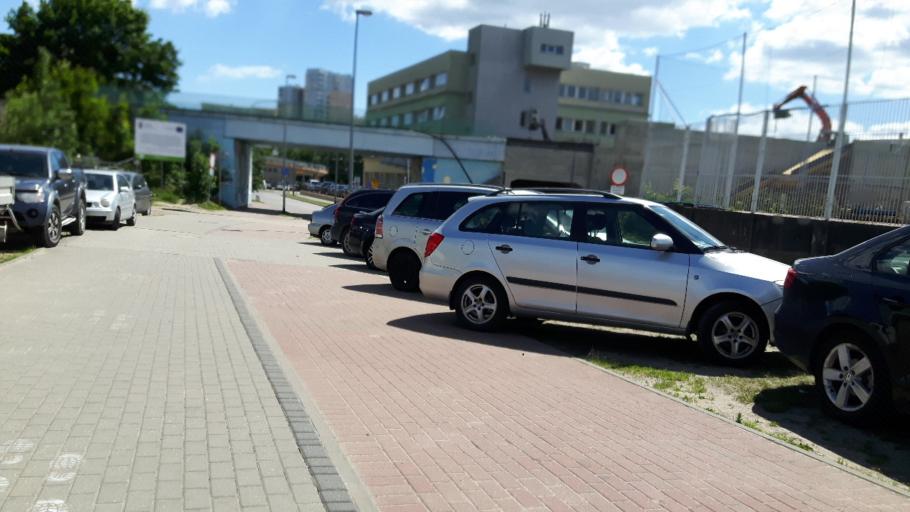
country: PL
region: Pomeranian Voivodeship
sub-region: Gdynia
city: Gdynia
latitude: 54.4968
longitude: 18.5326
